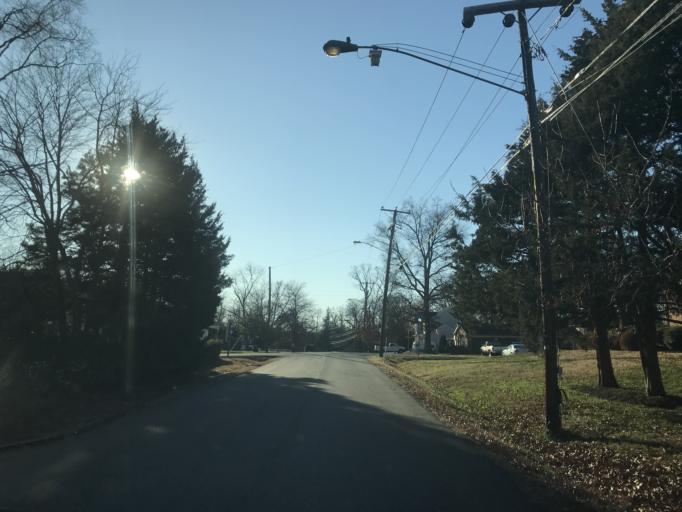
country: US
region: Virginia
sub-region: Fairfax County
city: Franconia
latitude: 38.7914
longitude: -77.1497
